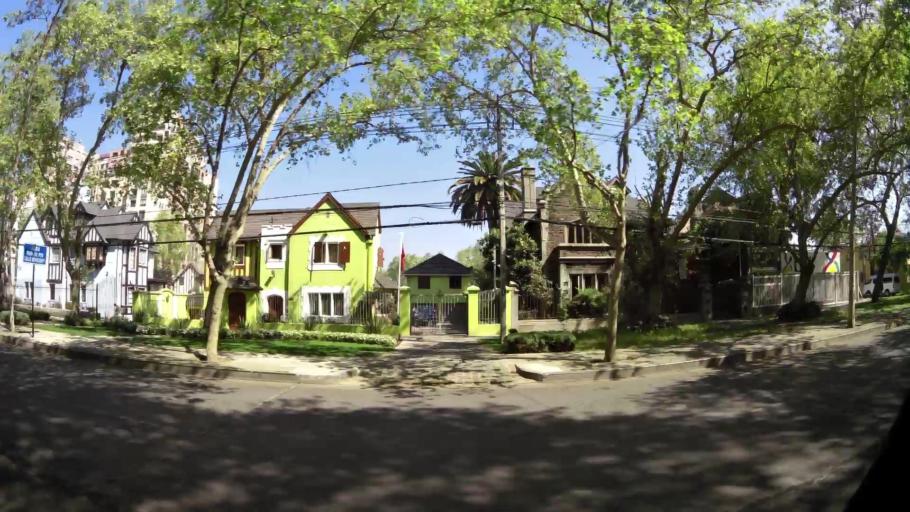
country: CL
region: Santiago Metropolitan
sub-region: Provincia de Santiago
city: Santiago
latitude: -33.4667
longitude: -70.6636
